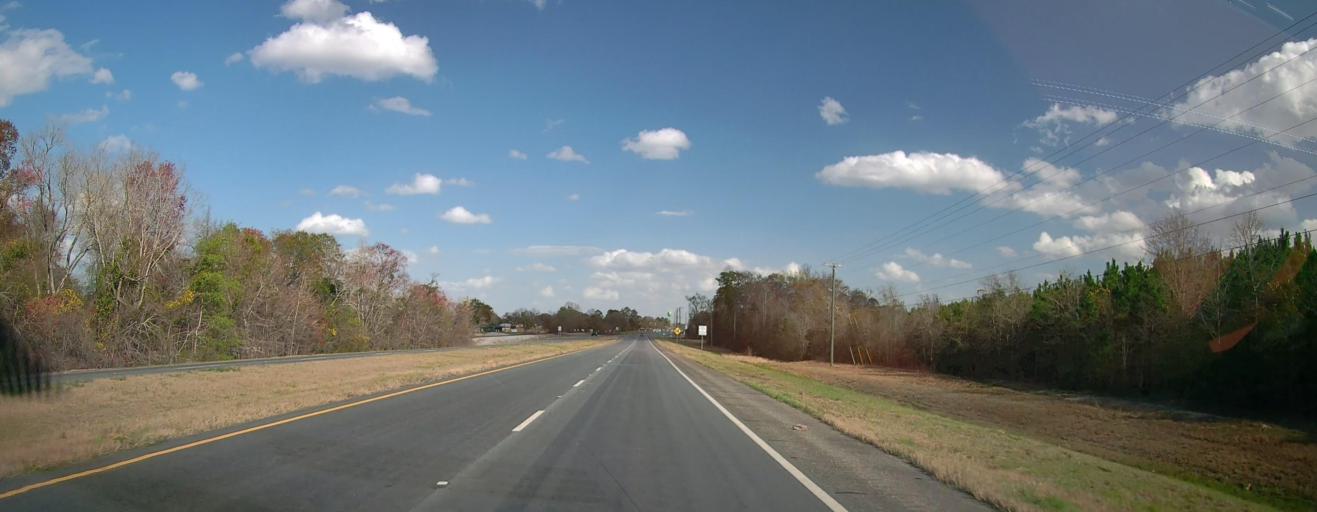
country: US
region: Georgia
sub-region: Dodge County
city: Eastman
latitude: 32.1072
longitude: -83.0796
